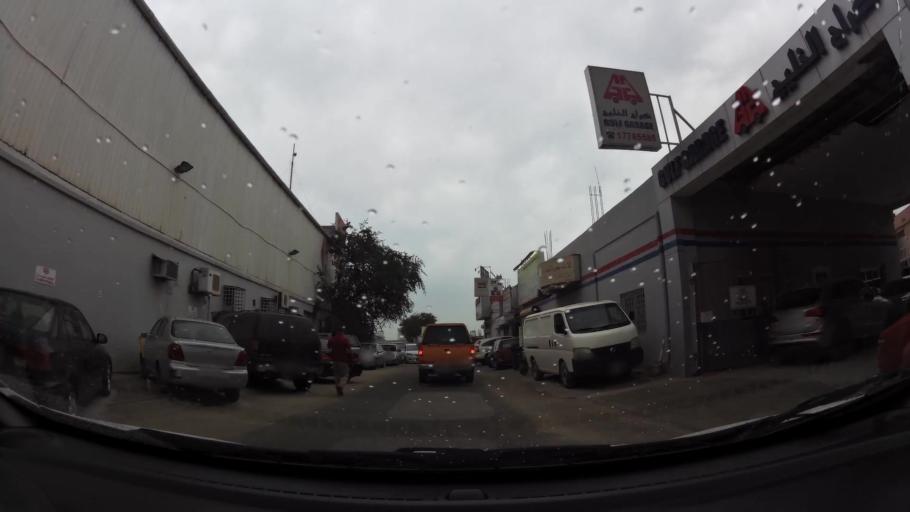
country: BH
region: Northern
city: Madinat `Isa
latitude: 26.1863
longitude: 50.5330
